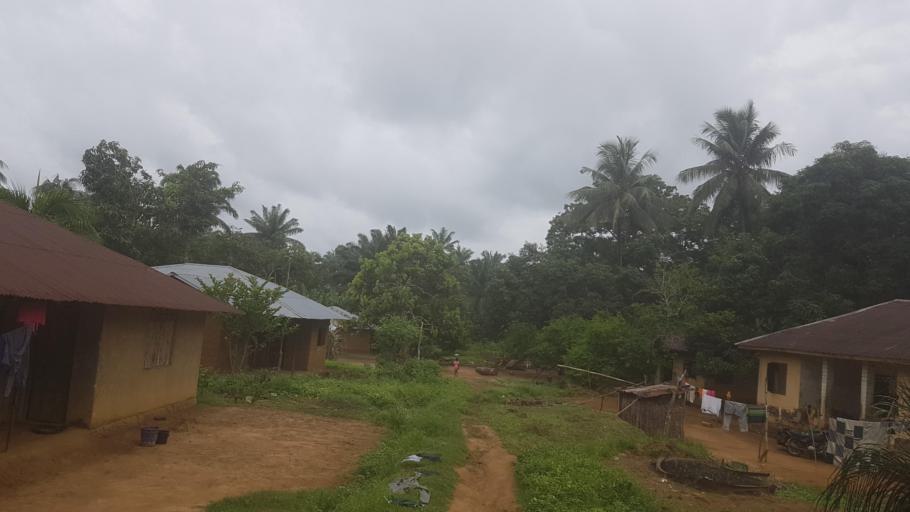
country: SL
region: Southern Province
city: Sumbuya
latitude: 7.5346
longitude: -12.1785
